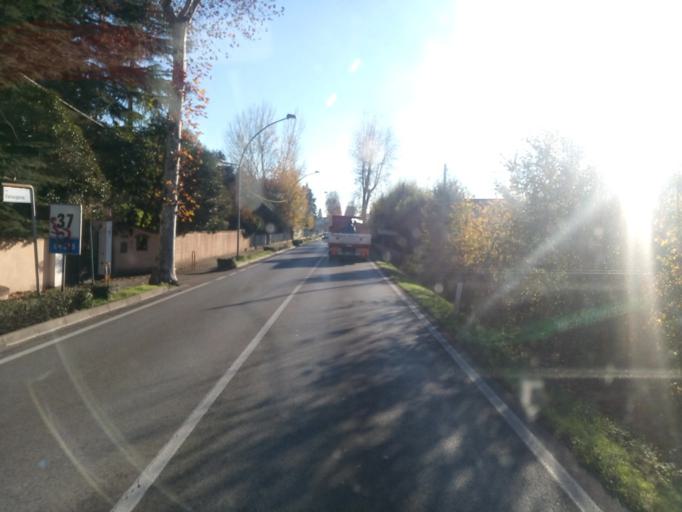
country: IT
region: Veneto
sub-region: Provincia di Treviso
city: Castello di Godego
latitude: 45.6830
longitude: 11.8976
